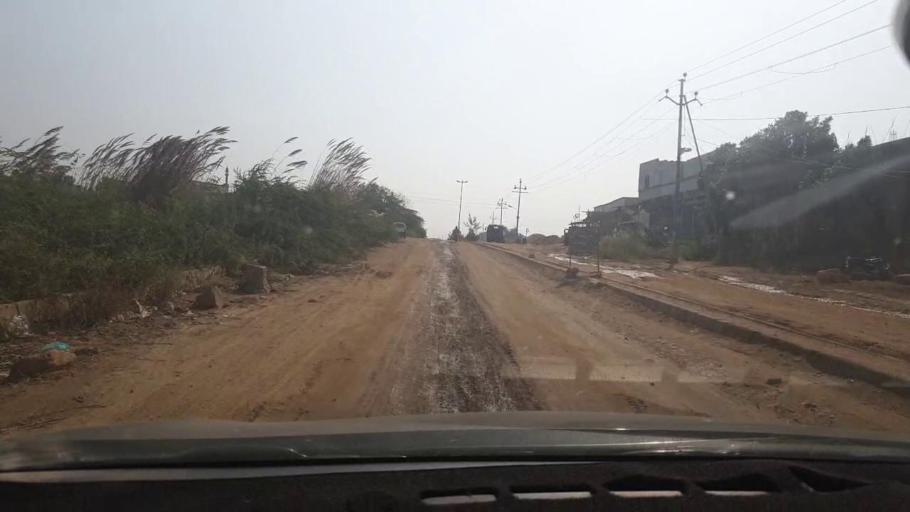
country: PK
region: Sindh
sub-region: Karachi District
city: Karachi
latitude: 25.0013
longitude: 66.9719
